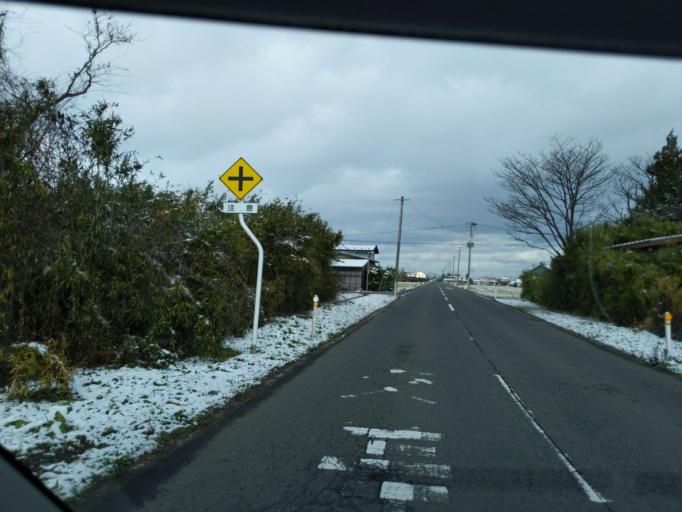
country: JP
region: Iwate
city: Mizusawa
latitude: 39.1582
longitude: 141.1119
